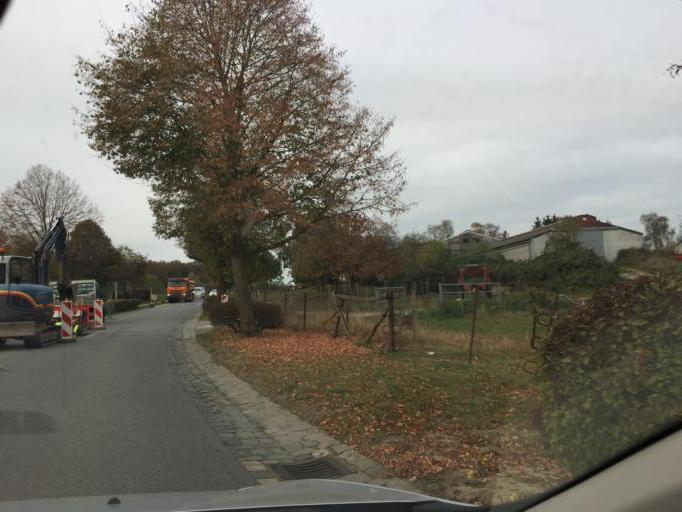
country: LU
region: Luxembourg
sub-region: Canton de Capellen
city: Kehlen
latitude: 49.6666
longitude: 6.0283
